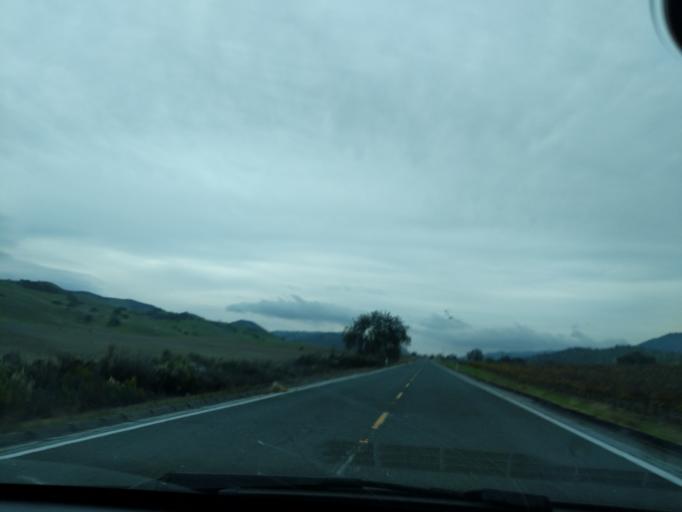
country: US
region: California
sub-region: San Benito County
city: Ridgemark
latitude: 36.6906
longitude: -121.2664
